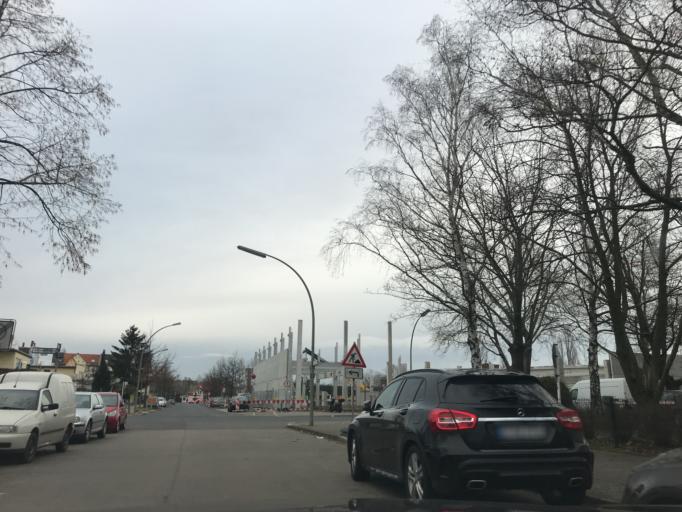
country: DE
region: Berlin
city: Wilhelmstadt
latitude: 52.5321
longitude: 13.1882
